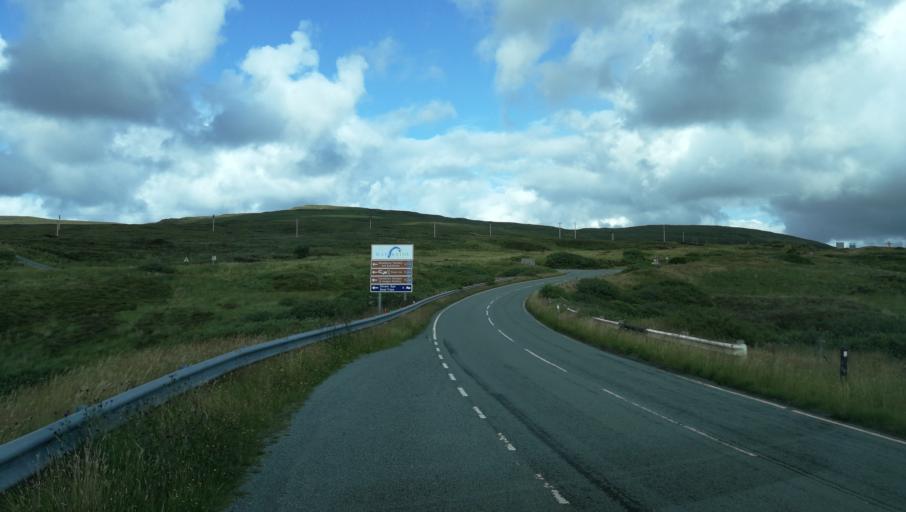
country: GB
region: Scotland
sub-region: Highland
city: Isle of Skye
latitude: 57.4692
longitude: -6.5396
